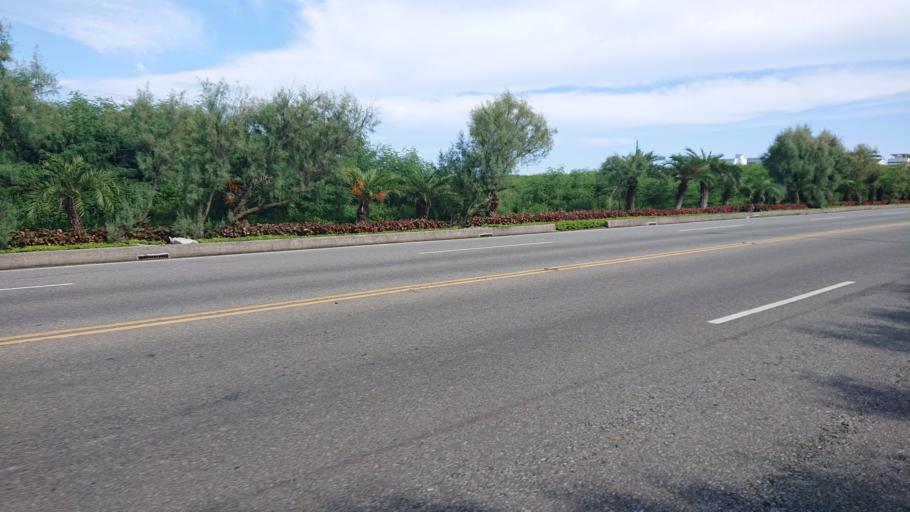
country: TW
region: Taiwan
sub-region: Penghu
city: Ma-kung
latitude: 23.5390
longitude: 119.6044
